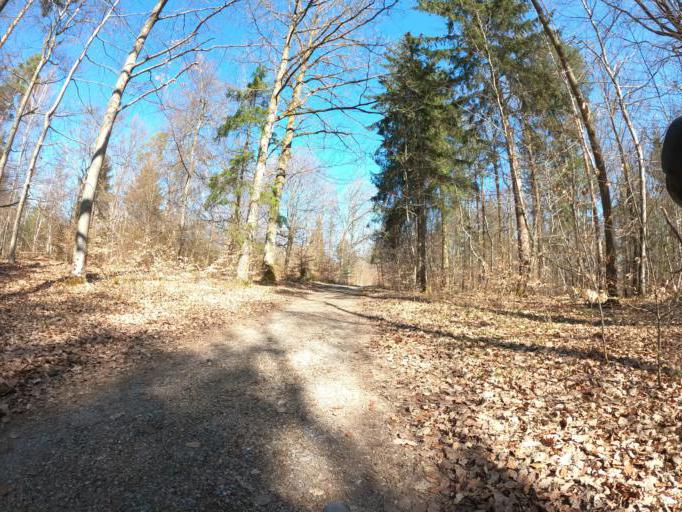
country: DE
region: Baden-Wuerttemberg
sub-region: Tuebingen Region
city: Rangendingen
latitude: 48.3921
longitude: 8.9032
